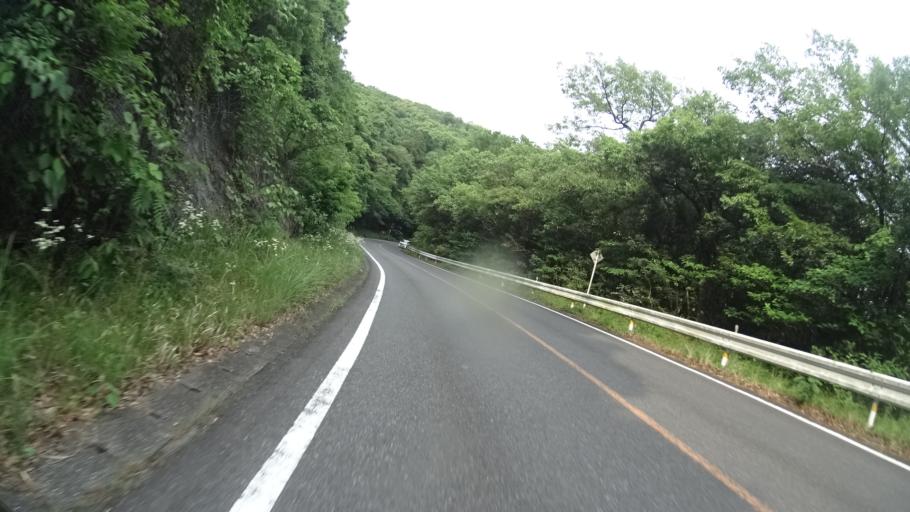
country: JP
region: Yamaguchi
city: Ogori-shimogo
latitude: 34.2277
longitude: 131.3072
